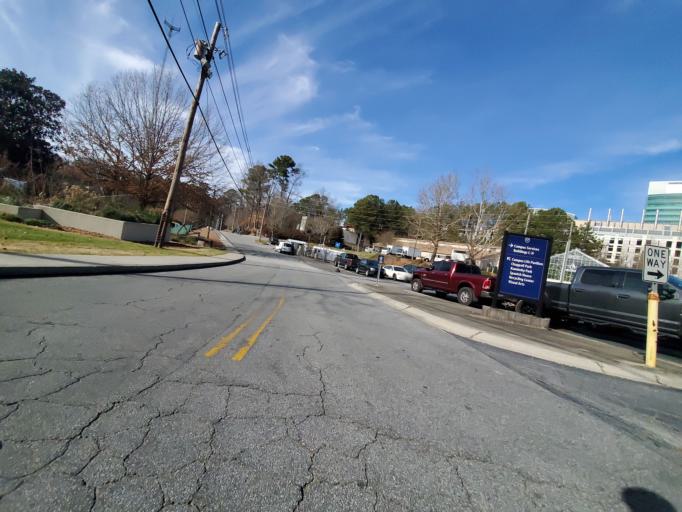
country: US
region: Georgia
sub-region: DeKalb County
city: Druid Hills
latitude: 33.7956
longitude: -84.3278
